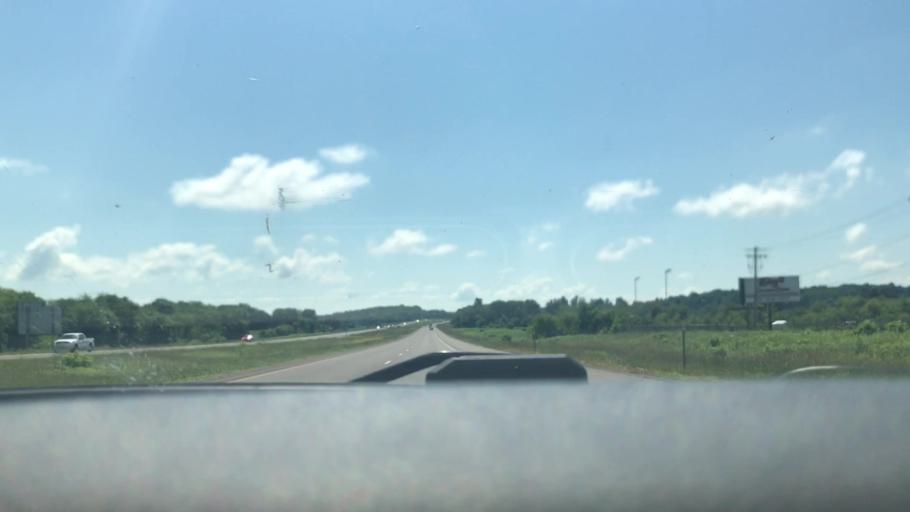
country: US
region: Wisconsin
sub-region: Chippewa County
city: Bloomer
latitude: 45.0964
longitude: -91.4996
